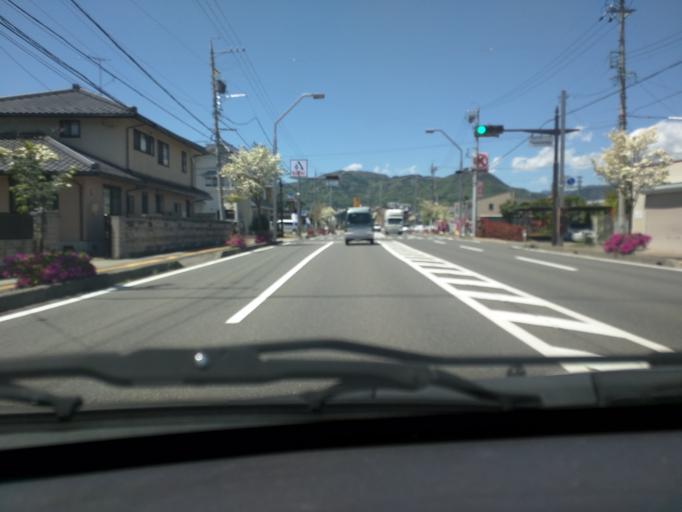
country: JP
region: Nagano
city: Nagano-shi
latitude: 36.6424
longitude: 138.2067
